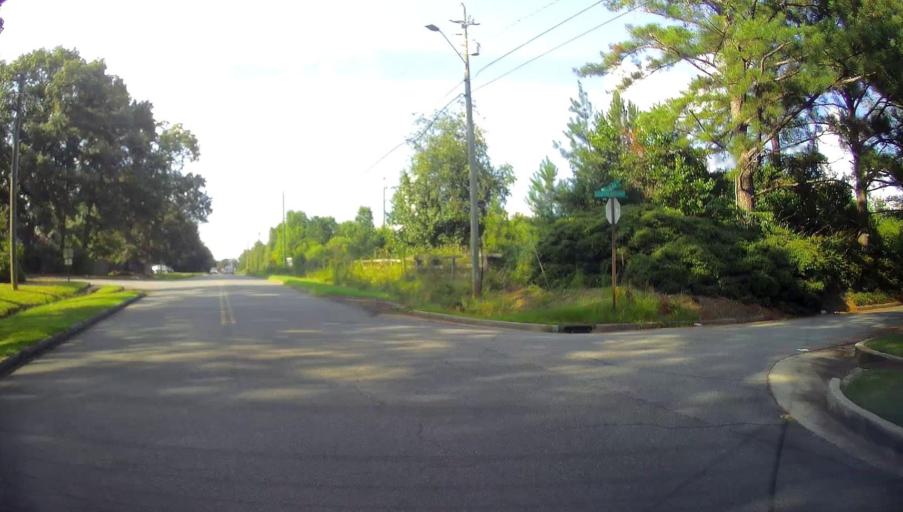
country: US
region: Georgia
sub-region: Houston County
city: Warner Robins
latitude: 32.5884
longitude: -83.6326
